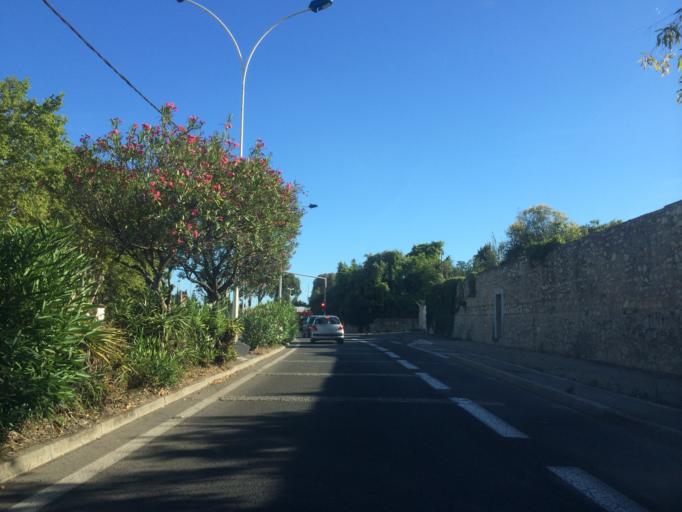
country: FR
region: Provence-Alpes-Cote d'Azur
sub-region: Departement des Alpes-Maritimes
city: Antibes
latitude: 43.5916
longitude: 7.1245
